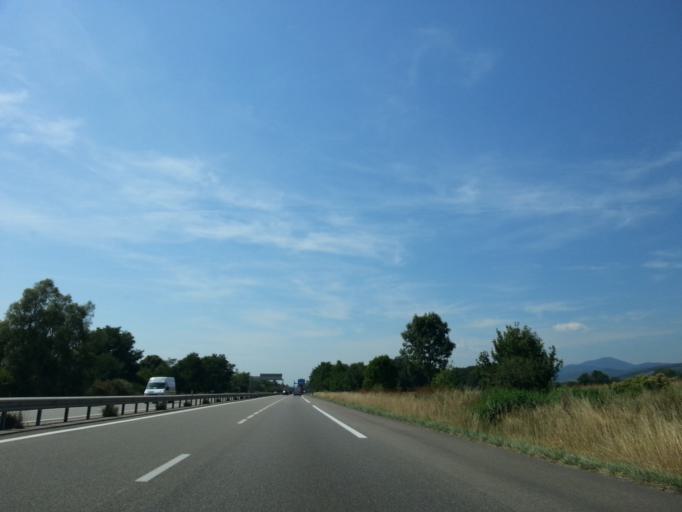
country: FR
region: Alsace
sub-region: Departement du Bas-Rhin
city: Niedernai
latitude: 48.4399
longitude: 7.5008
